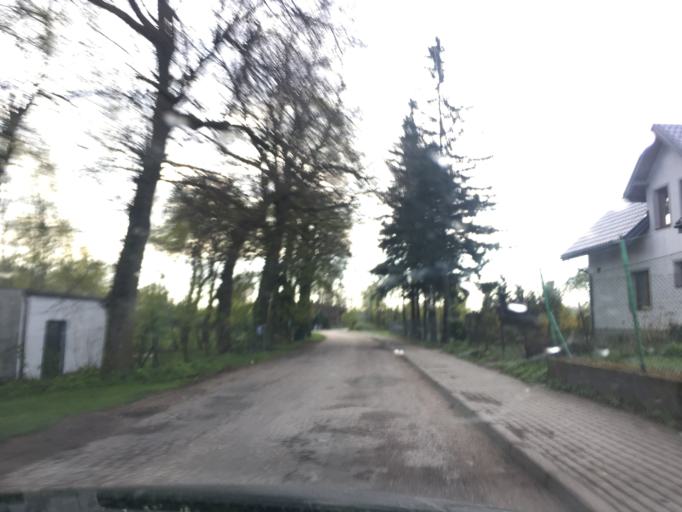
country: PL
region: Warmian-Masurian Voivodeship
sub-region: Powiat ostrodzki
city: Dabrowno
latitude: 53.4373
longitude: 19.9849
